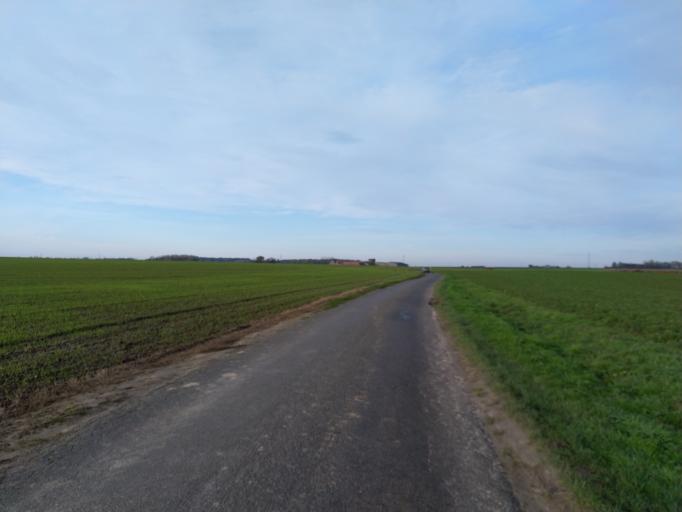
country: BE
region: Wallonia
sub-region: Province du Hainaut
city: Saint-Ghislain
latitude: 50.5188
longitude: 3.8362
